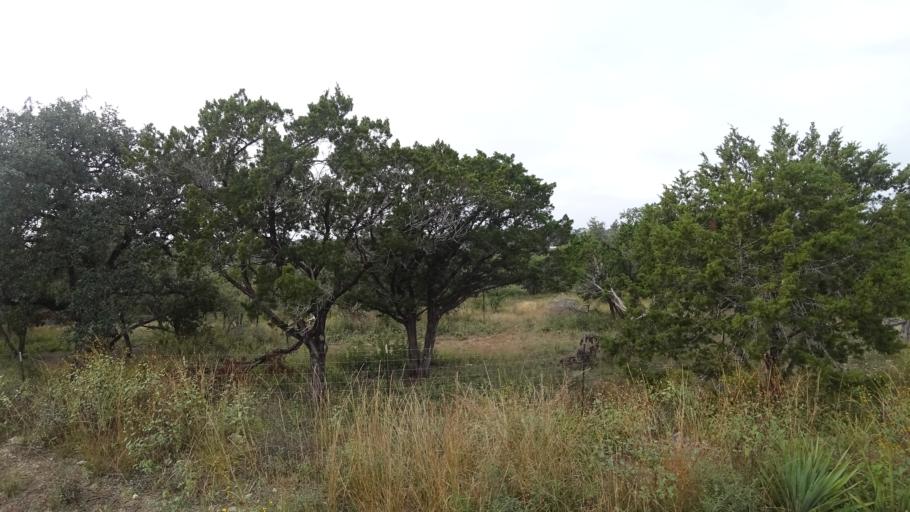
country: US
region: Texas
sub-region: Travis County
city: Hudson Bend
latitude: 30.3914
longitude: -97.9263
